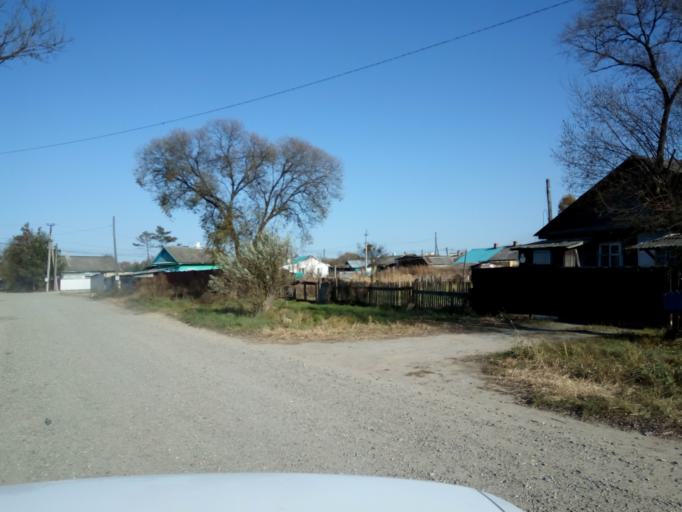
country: RU
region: Primorskiy
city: Dal'nerechensk
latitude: 45.9196
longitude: 133.7225
